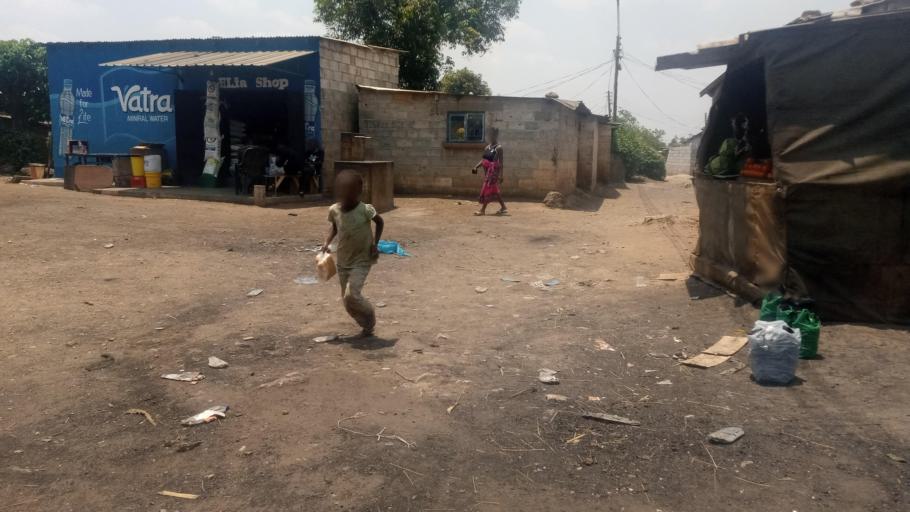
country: ZM
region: Lusaka
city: Lusaka
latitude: -15.4471
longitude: 28.3749
